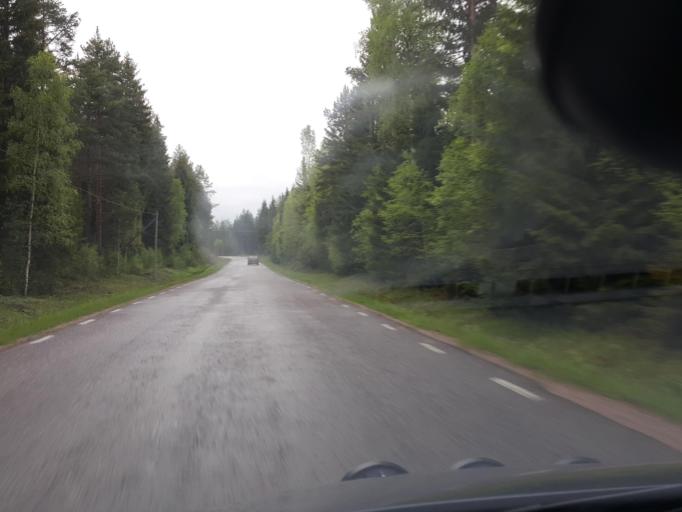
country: SE
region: Gaevleborg
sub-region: Ljusdals Kommun
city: Jaervsoe
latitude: 61.7612
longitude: 16.2052
